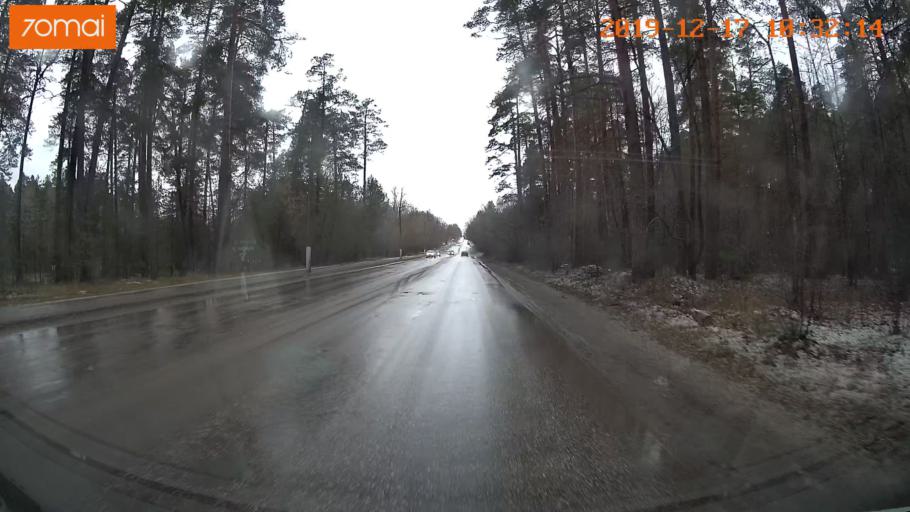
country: RU
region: Vladimir
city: Gus'-Khrustal'nyy
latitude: 55.6302
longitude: 40.6906
